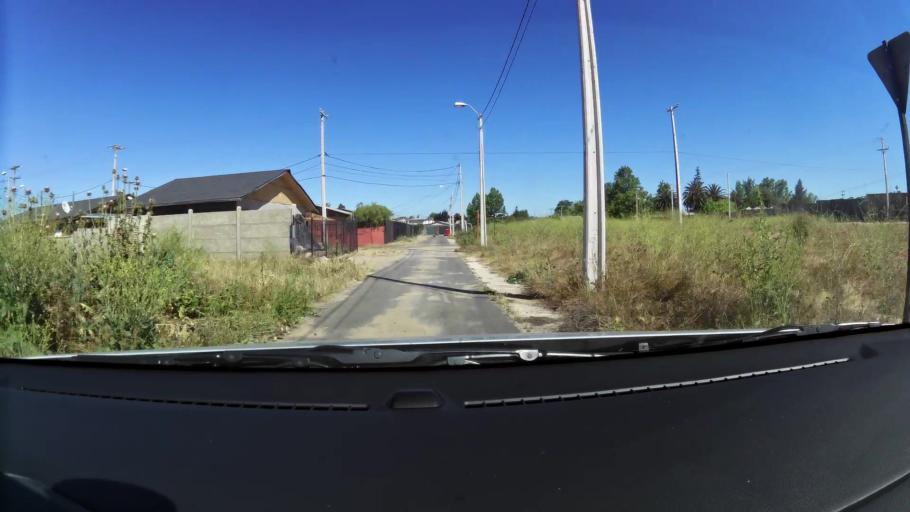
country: CL
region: Valparaiso
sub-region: Provincia de Marga Marga
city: Quilpue
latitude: -33.3217
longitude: -71.3960
